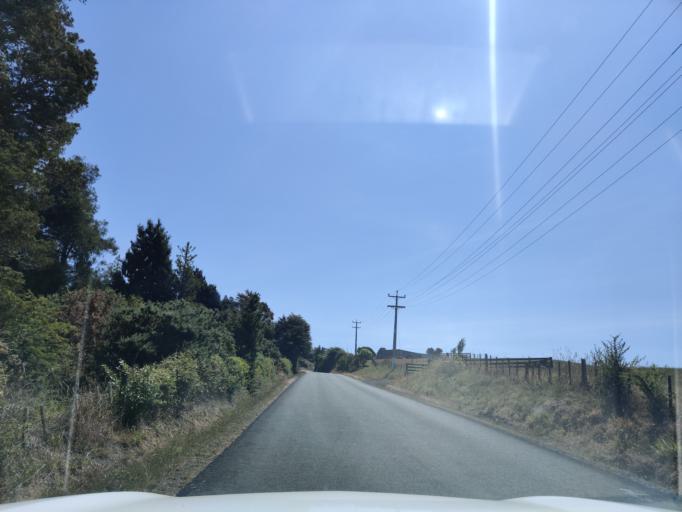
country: NZ
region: Auckland
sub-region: Auckland
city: Red Hill
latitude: -37.0630
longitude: 175.0820
